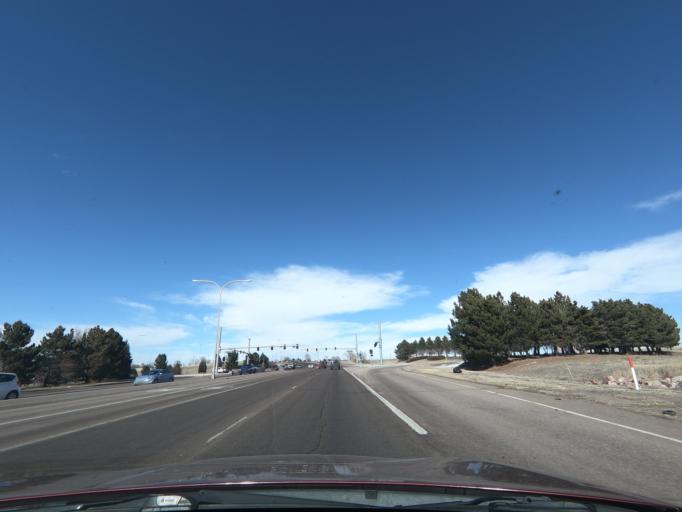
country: US
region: Colorado
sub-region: El Paso County
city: Security-Widefield
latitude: 38.7802
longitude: -104.7206
